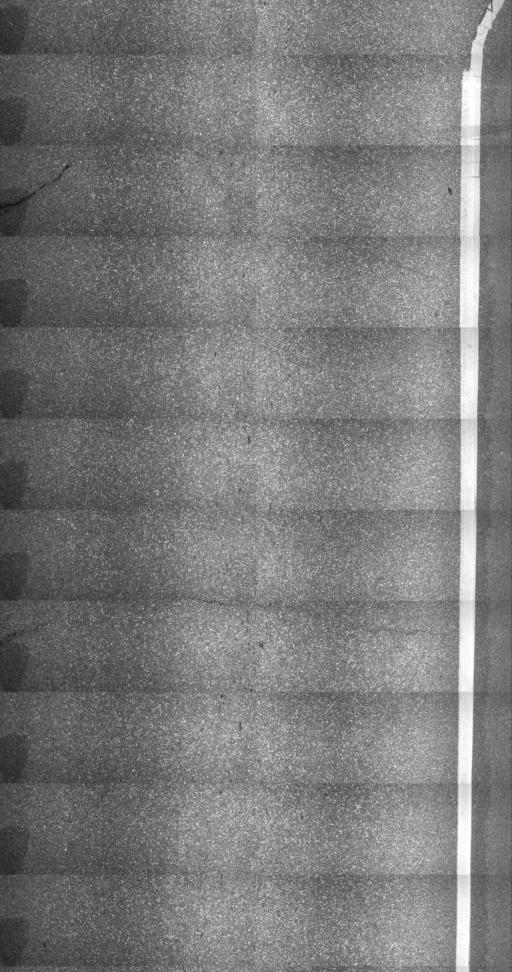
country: US
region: Vermont
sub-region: Washington County
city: Waterbury
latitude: 44.3439
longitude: -72.7500
